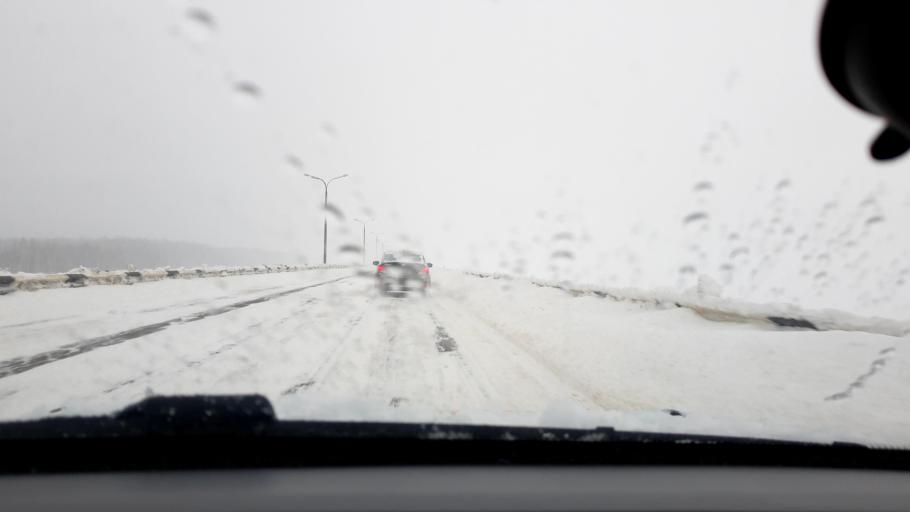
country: RU
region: Nizjnij Novgorod
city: Pervomayskiy
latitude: 56.6428
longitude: 43.3153
